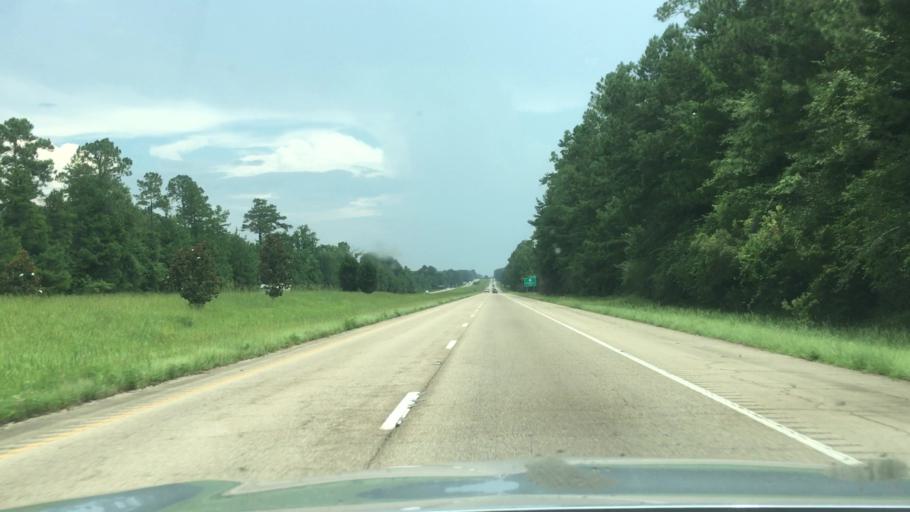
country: US
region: Mississippi
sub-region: Lamar County
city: Lumberton
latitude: 30.9835
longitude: -89.4273
